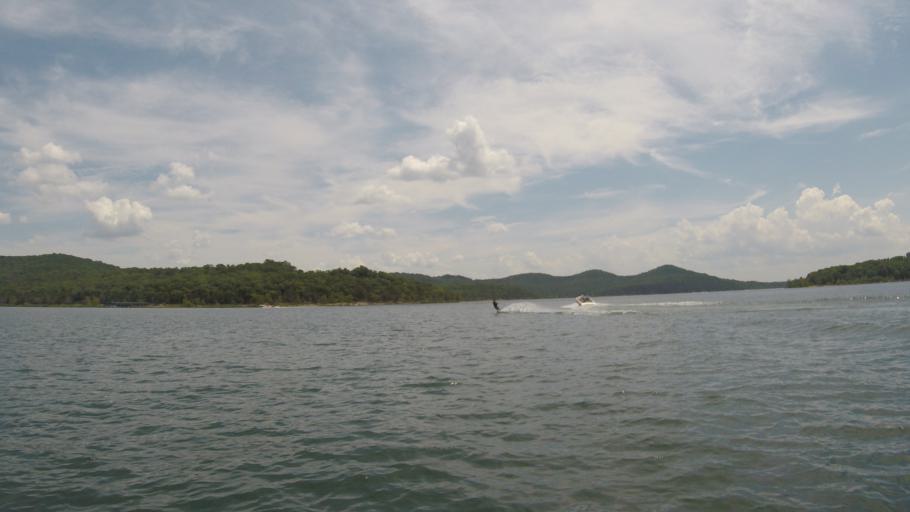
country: US
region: Missouri
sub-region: Barry County
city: Shell Knob
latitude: 36.6180
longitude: -93.5475
